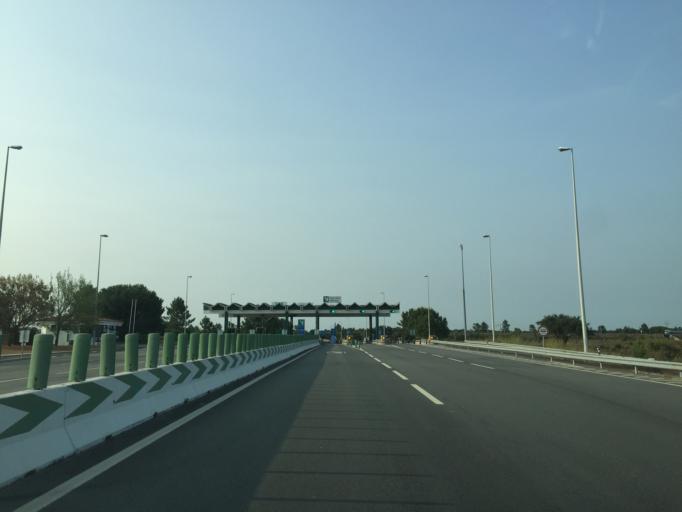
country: PT
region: Setubal
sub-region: Setubal
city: Setubal
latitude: 38.5968
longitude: -8.6735
